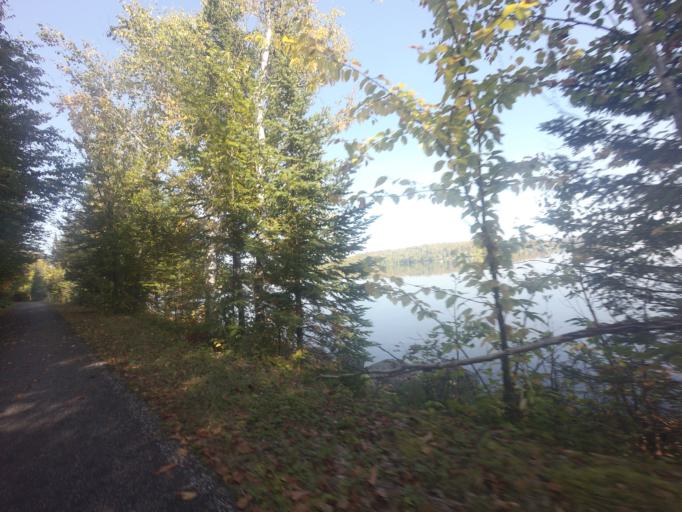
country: CA
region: Quebec
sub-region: Laurentides
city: Mont-Laurier
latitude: 46.5183
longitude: -75.4273
